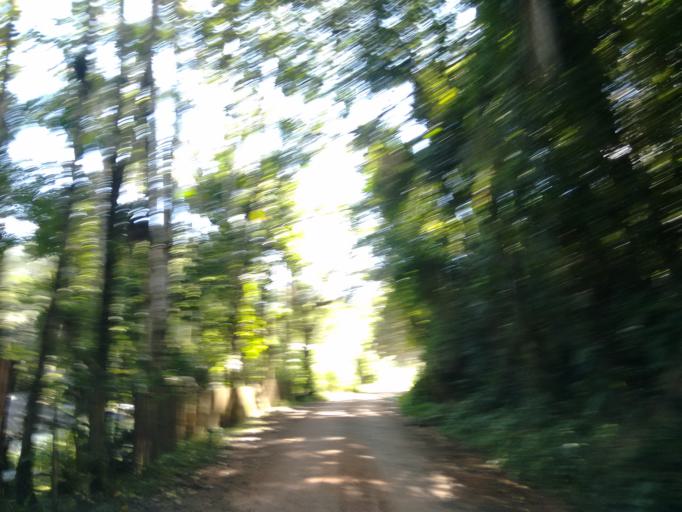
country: BR
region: Santa Catarina
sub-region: Indaial
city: Indaial
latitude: -26.9377
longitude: -49.1809
